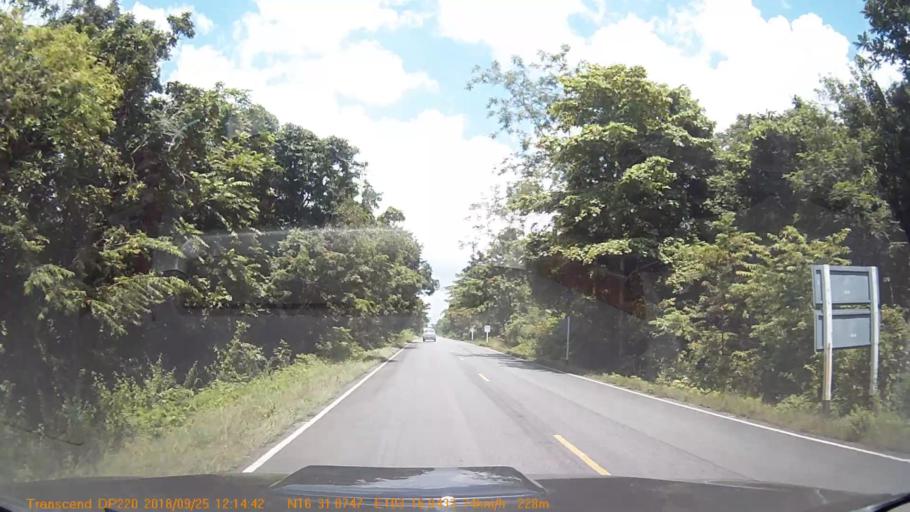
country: TH
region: Kalasin
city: Huai Mek
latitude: 16.5180
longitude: 103.2674
